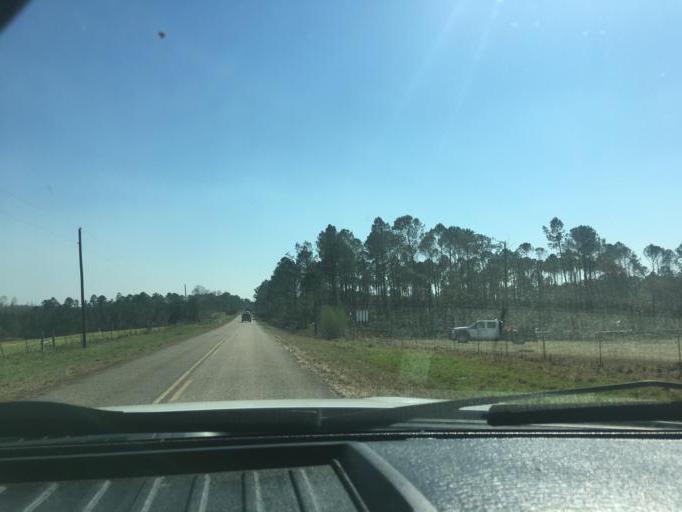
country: US
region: Alabama
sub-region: Lee County
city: Auburn
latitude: 32.4657
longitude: -85.4027
